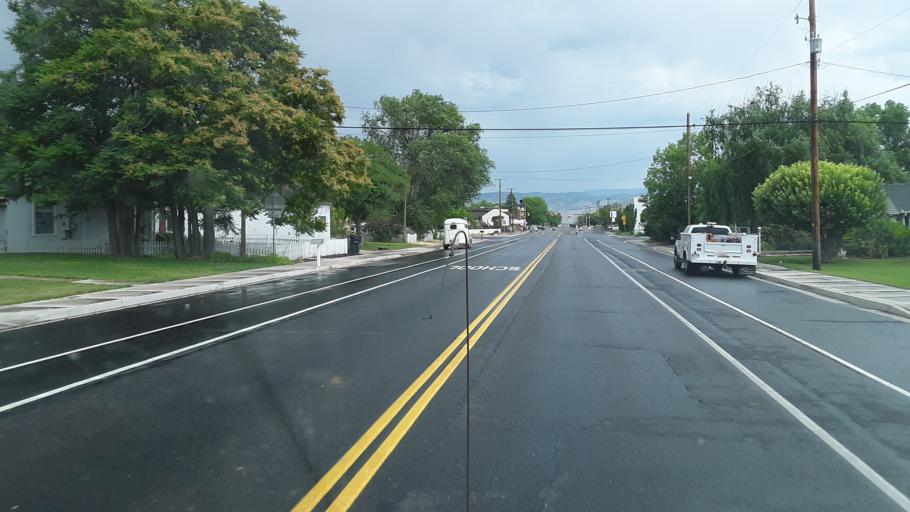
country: US
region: Utah
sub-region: Sevier County
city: Richfield
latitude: 38.7723
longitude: -112.0879
